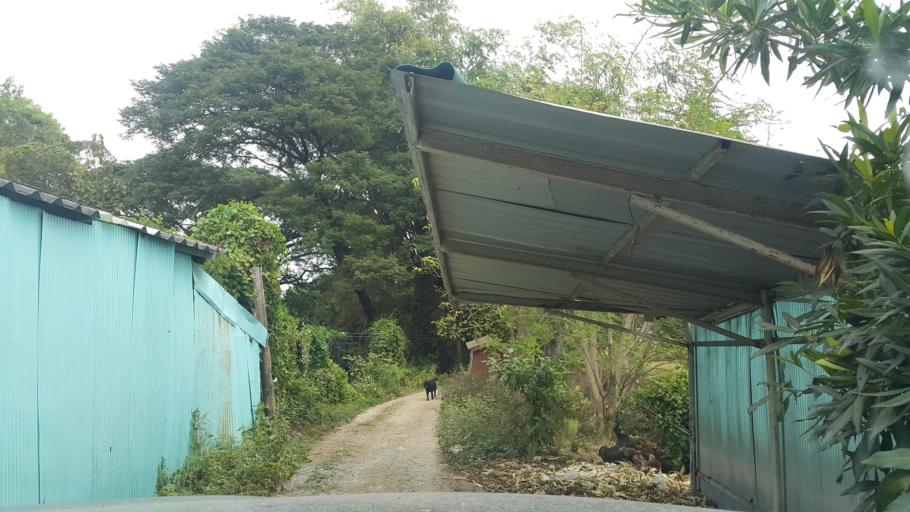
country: TH
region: Chiang Mai
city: Chiang Mai
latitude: 18.7933
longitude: 99.0333
